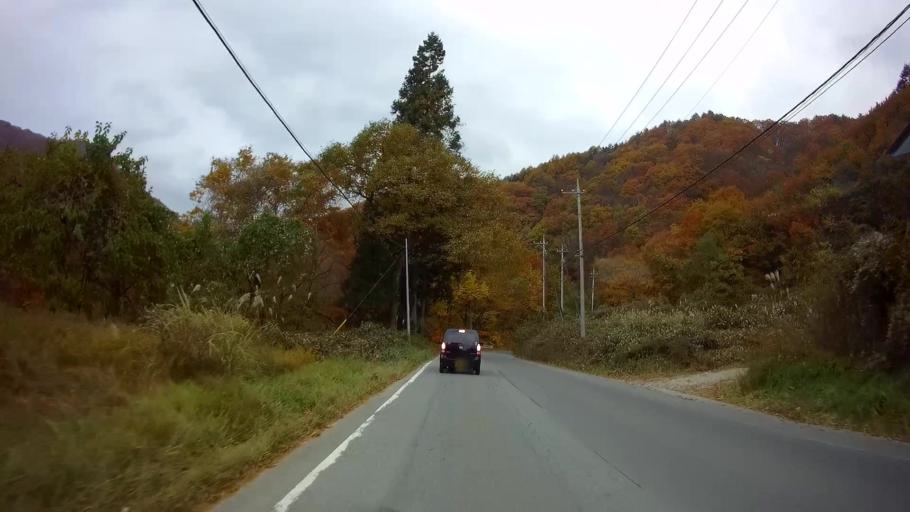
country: JP
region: Gunma
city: Nakanojomachi
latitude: 36.6263
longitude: 138.6485
